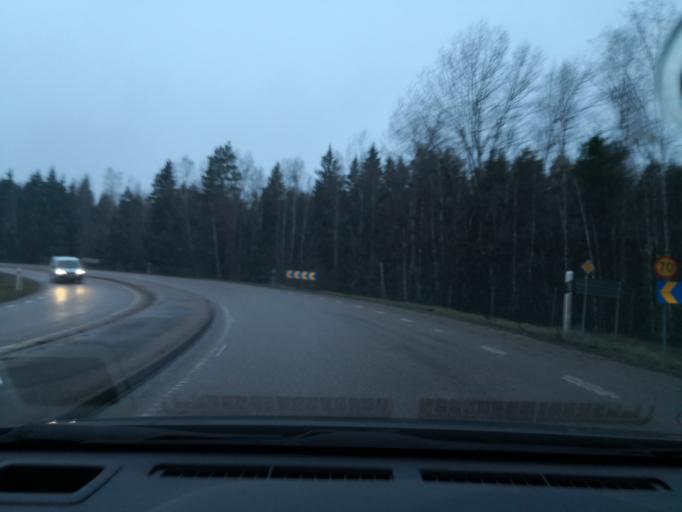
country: SE
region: Vaestmanland
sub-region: Hallstahammars Kommun
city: Kolback
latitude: 59.5824
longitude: 16.3544
